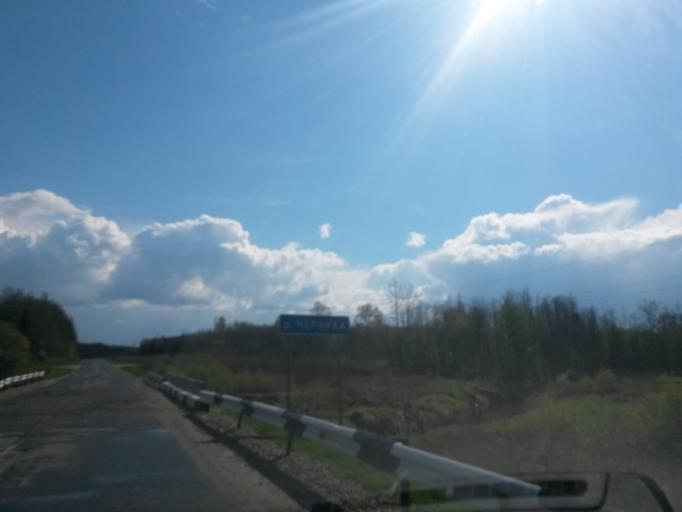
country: RU
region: Jaroslavl
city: Tutayev
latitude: 57.9643
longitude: 39.5038
